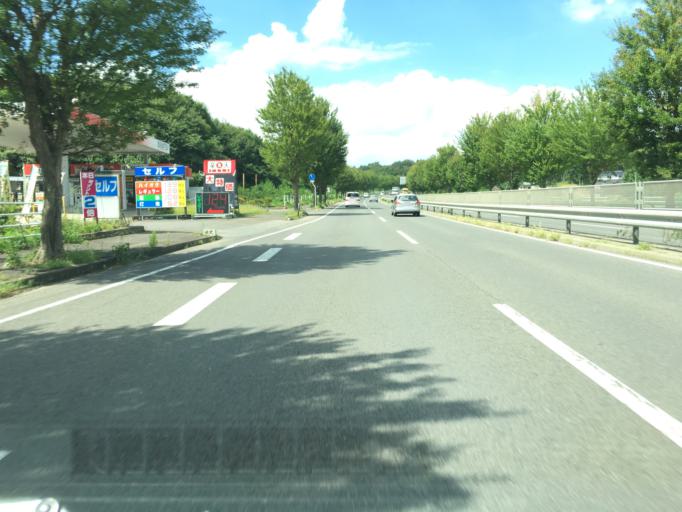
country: JP
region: Fukushima
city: Fukushima-shi
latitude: 37.6857
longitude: 140.4682
